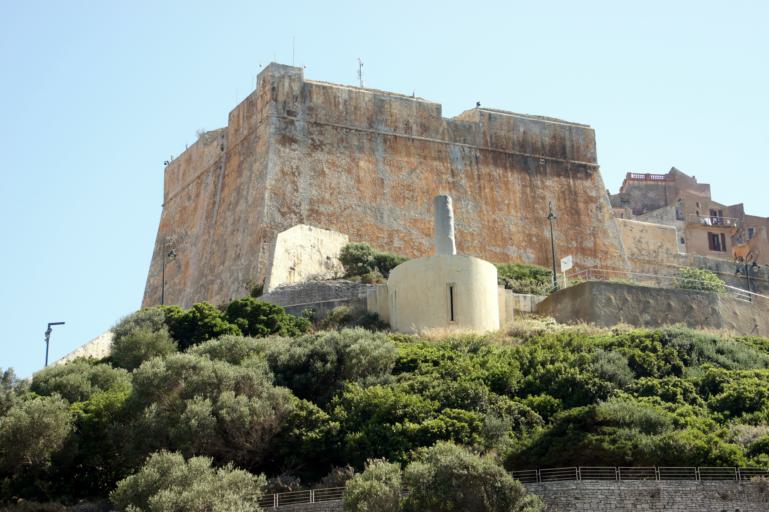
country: FR
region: Corsica
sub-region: Departement de la Corse-du-Sud
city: Bonifacio
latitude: 41.3883
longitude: 9.1647
